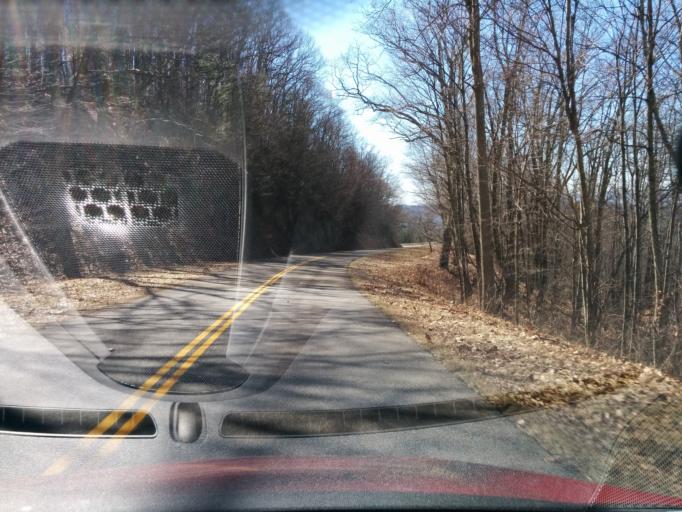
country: US
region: Virginia
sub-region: City of Buena Vista
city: Buena Vista
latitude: 37.8015
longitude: -79.1935
